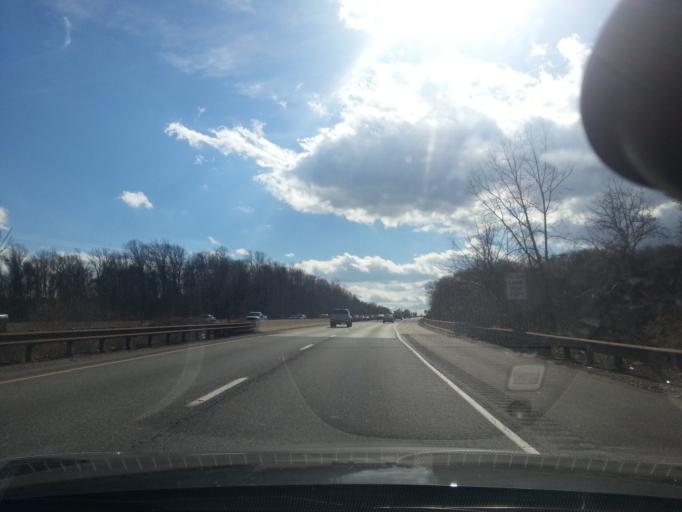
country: US
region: Pennsylvania
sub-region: Delaware County
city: Springfield
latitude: 39.9553
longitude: -75.3364
